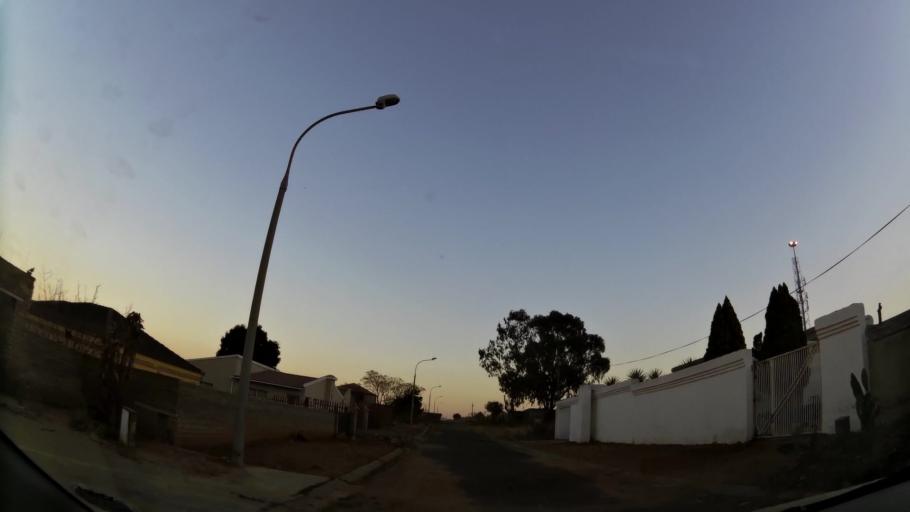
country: ZA
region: Gauteng
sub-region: West Rand District Municipality
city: Randfontein
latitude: -26.2044
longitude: 27.7198
